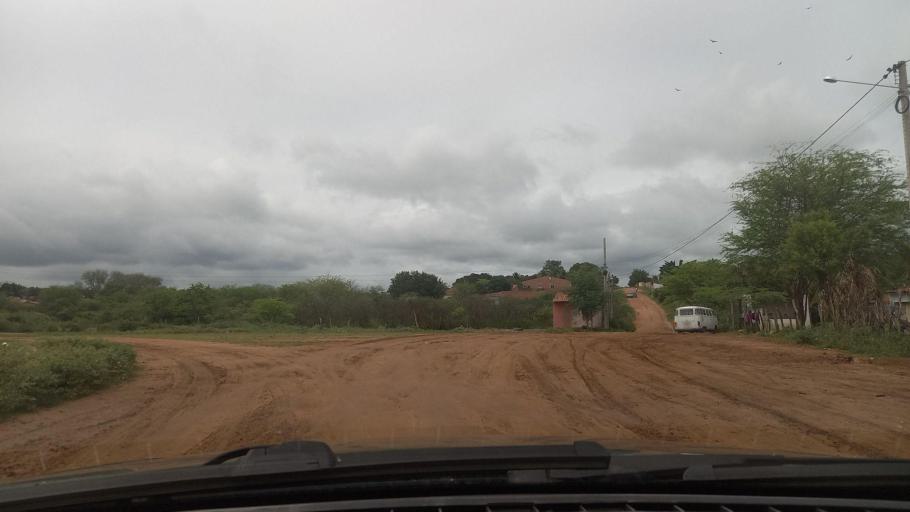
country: BR
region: Alagoas
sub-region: Delmiro Gouveia
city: Delmiro Gouveia
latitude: -9.3907
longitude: -37.9937
